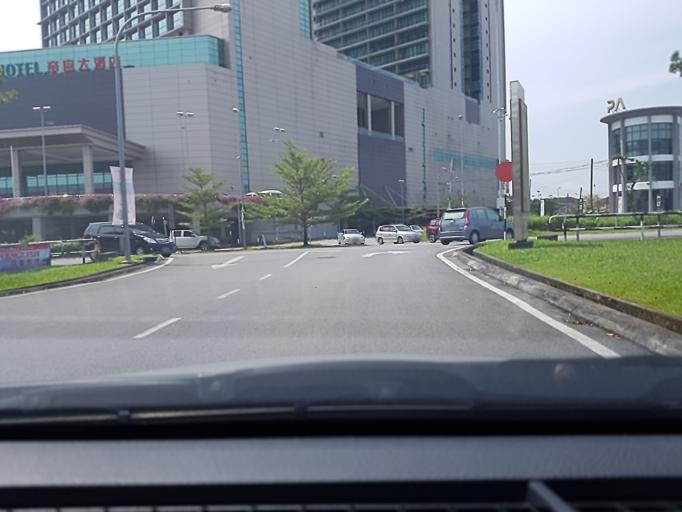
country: MY
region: Sarawak
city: Kuching
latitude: 1.5082
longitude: 110.3351
